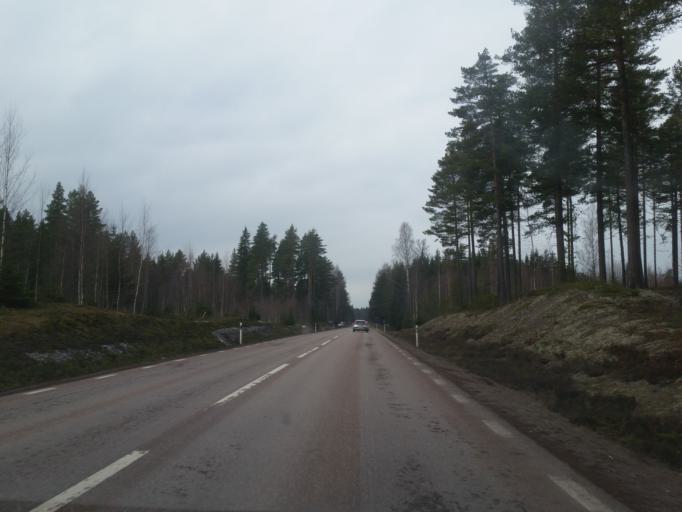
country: SE
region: Dalarna
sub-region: Mora Kommun
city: Mora
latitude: 61.0742
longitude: 14.3556
